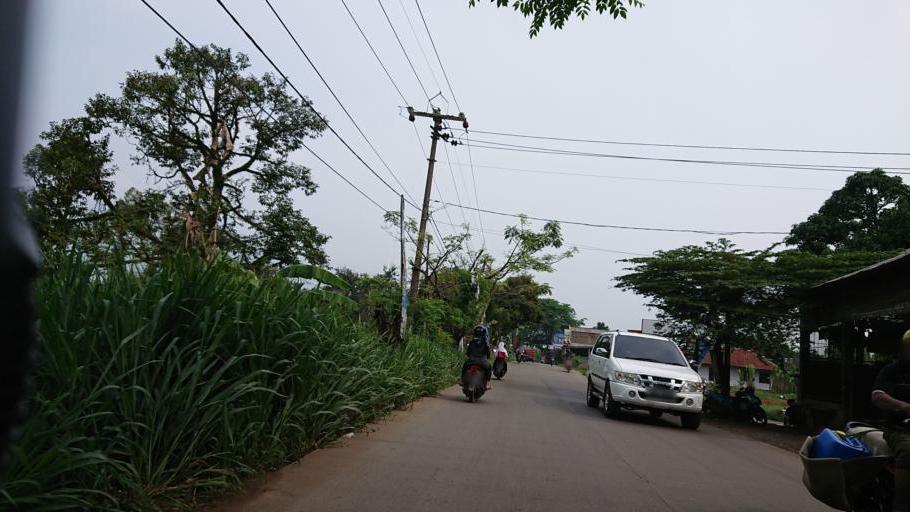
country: ID
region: West Java
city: Parung
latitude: -6.4068
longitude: 106.6940
